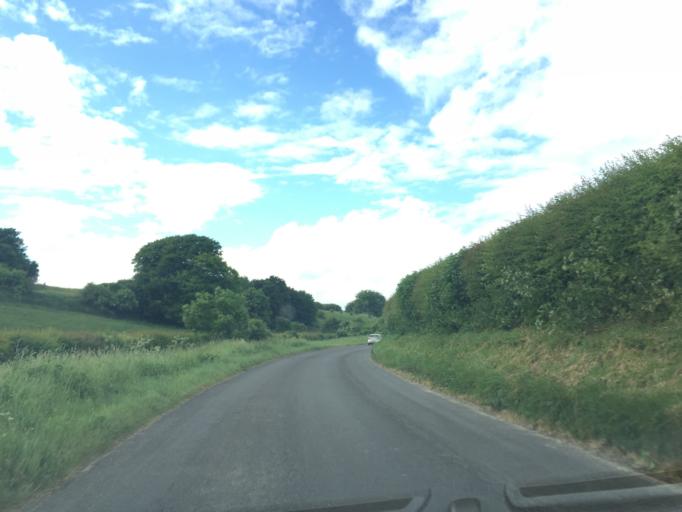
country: GB
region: England
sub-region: Dorset
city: Bovington Camp
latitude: 50.6547
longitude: -2.2742
